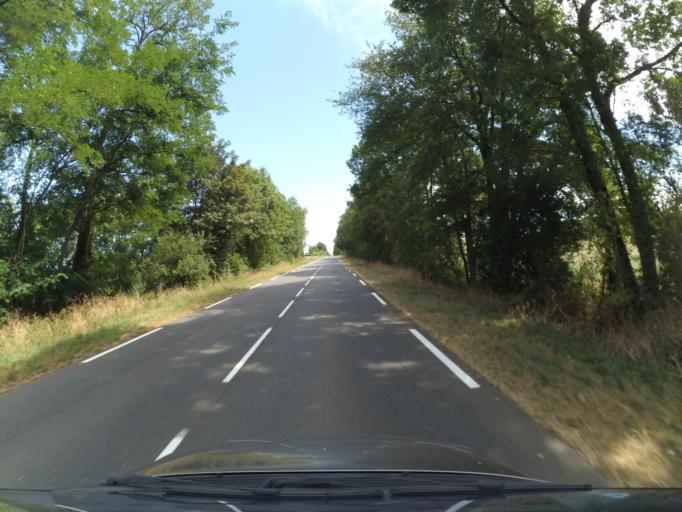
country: FR
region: Poitou-Charentes
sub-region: Departement de la Charente
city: Exideuil
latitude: 45.9531
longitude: 0.7108
